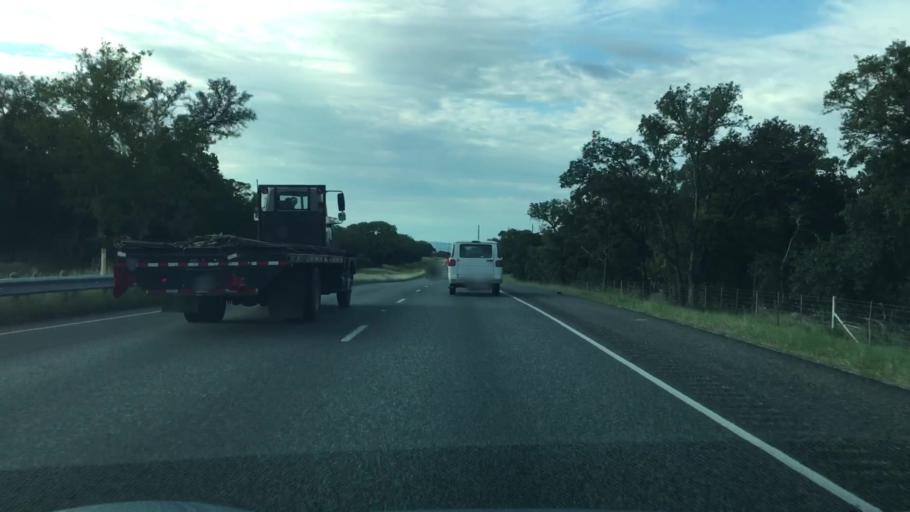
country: US
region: Texas
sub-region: Comal County
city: Canyon Lake
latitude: 29.9195
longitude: -98.4117
